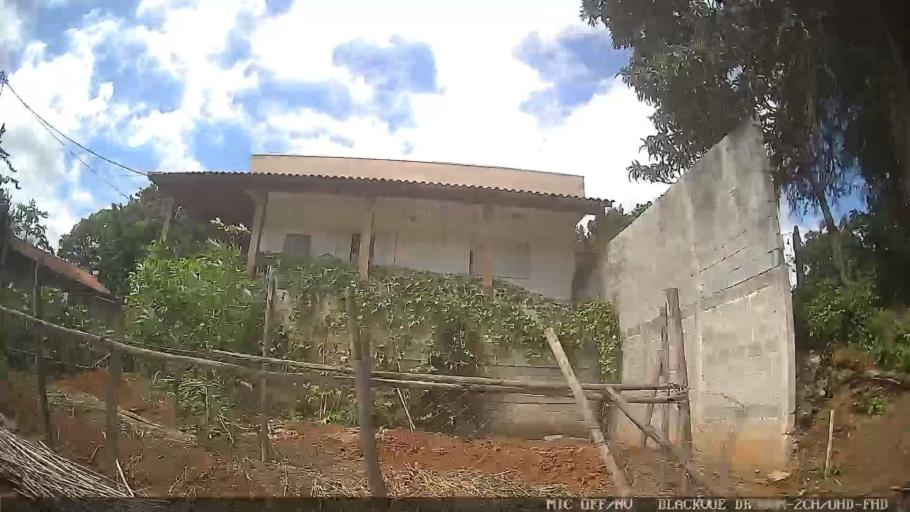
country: BR
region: Sao Paulo
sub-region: Amparo
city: Amparo
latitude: -22.8624
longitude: -46.7029
